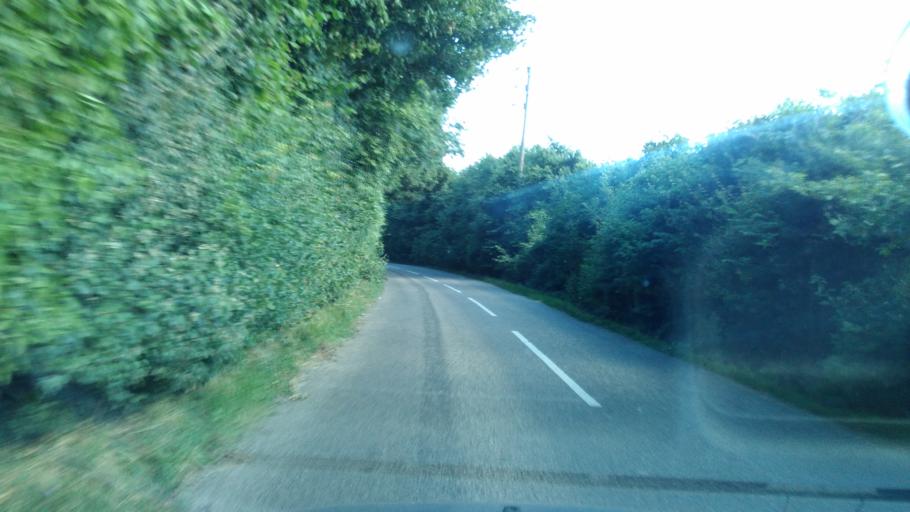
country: GB
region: England
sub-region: Kent
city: Dunkirk
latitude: 51.2535
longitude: 0.9575
